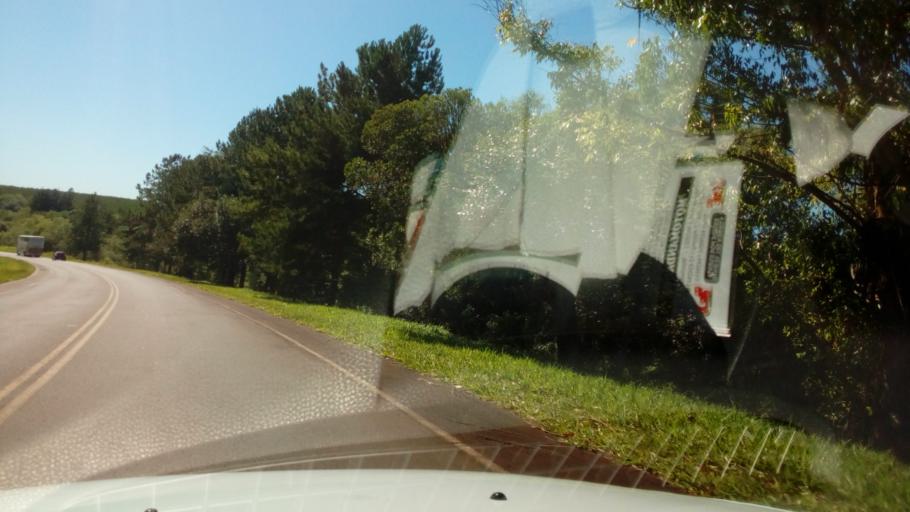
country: AR
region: Misiones
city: Santa Ana
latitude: -27.4175
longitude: -55.5373
